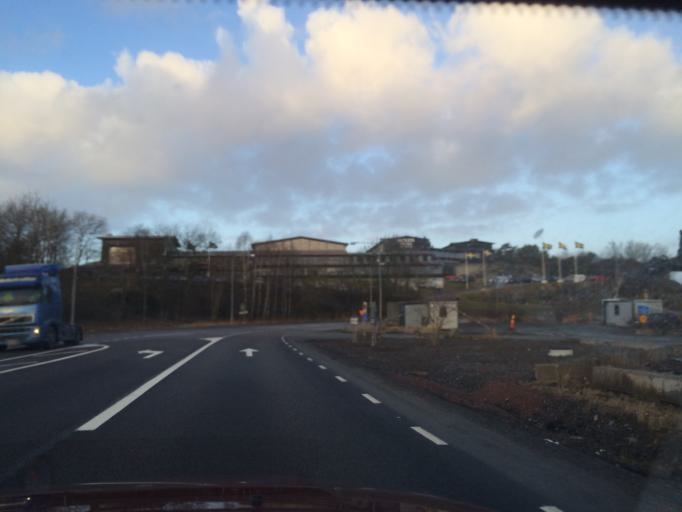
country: SE
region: Vaestra Goetaland
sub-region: Goteborg
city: Torslanda
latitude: 57.6960
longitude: 11.8308
